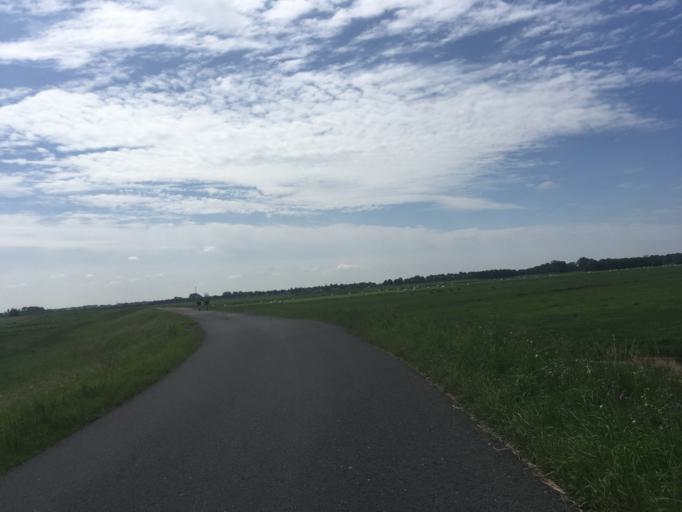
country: NL
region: North Holland
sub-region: Gemeente Haarlem
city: Haarlem
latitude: 52.3990
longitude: 4.7175
